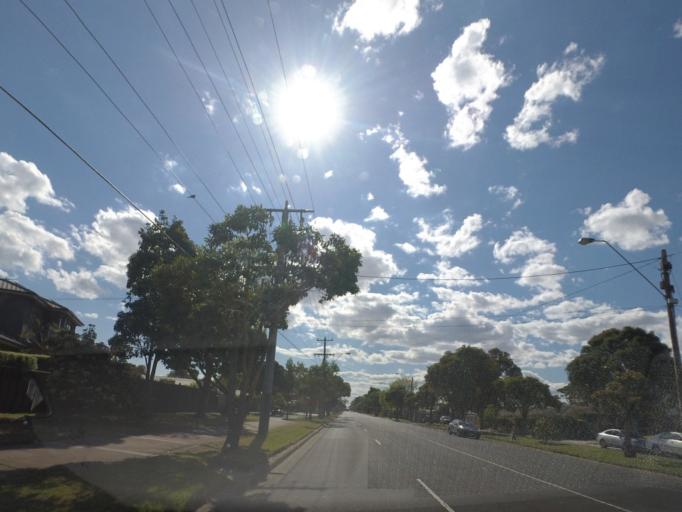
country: AU
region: Victoria
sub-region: Kingston
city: Dingley Village
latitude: -37.9861
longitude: 145.1366
